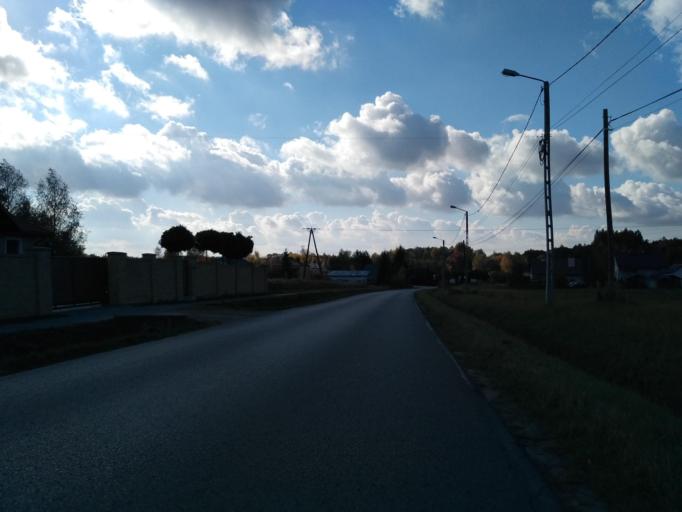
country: PL
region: Subcarpathian Voivodeship
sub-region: Powiat rzeszowski
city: Glogow Malopolski
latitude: 50.1454
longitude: 21.9498
